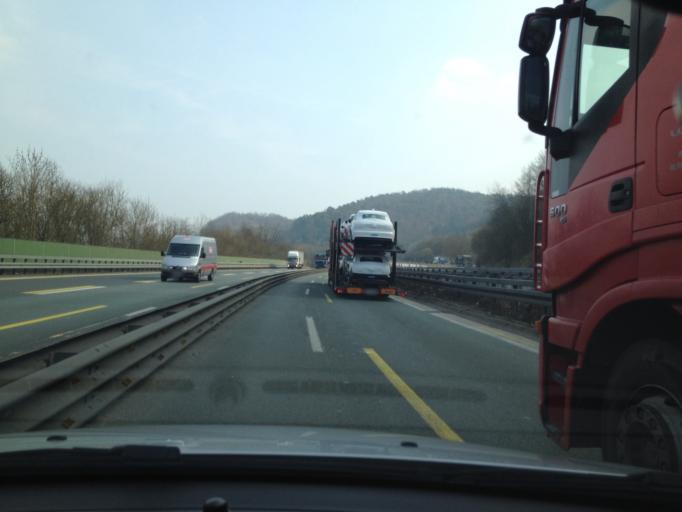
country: DE
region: Hesse
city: Dillenburg
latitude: 50.7451
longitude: 8.2538
